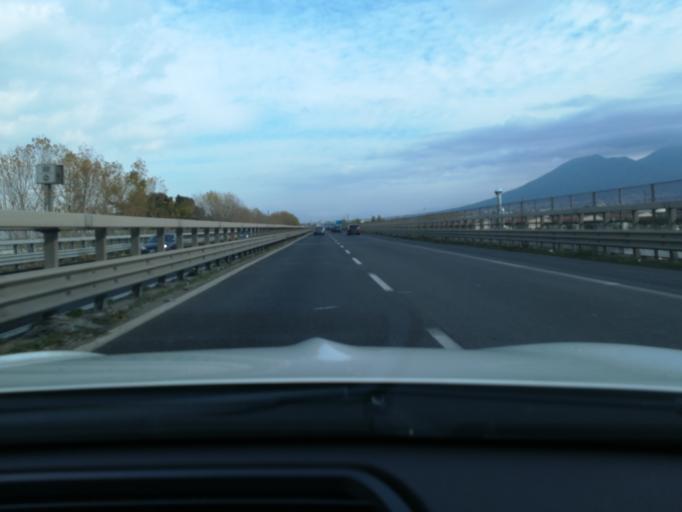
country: IT
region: Campania
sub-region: Provincia di Napoli
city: Arpino
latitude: 40.8648
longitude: 14.3028
